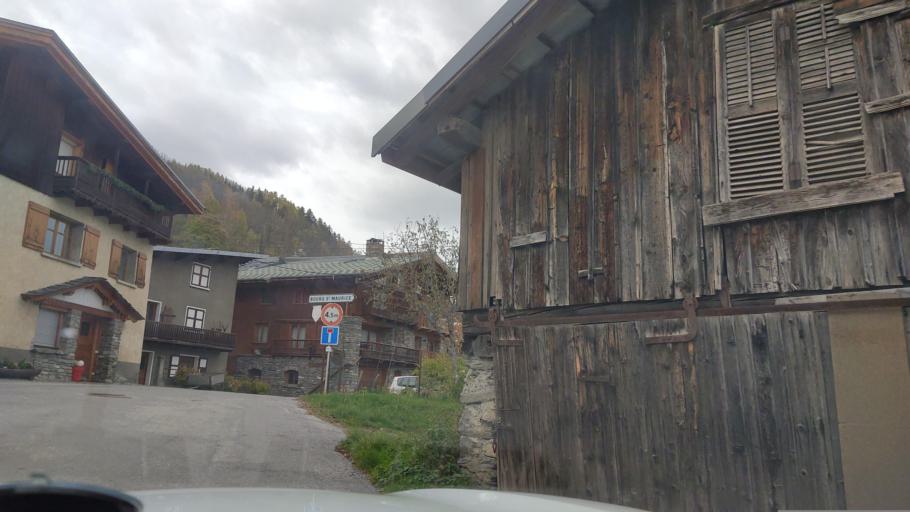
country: FR
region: Rhone-Alpes
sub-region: Departement de la Savoie
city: Bourg-Saint-Maurice
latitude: 45.6070
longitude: 6.7777
